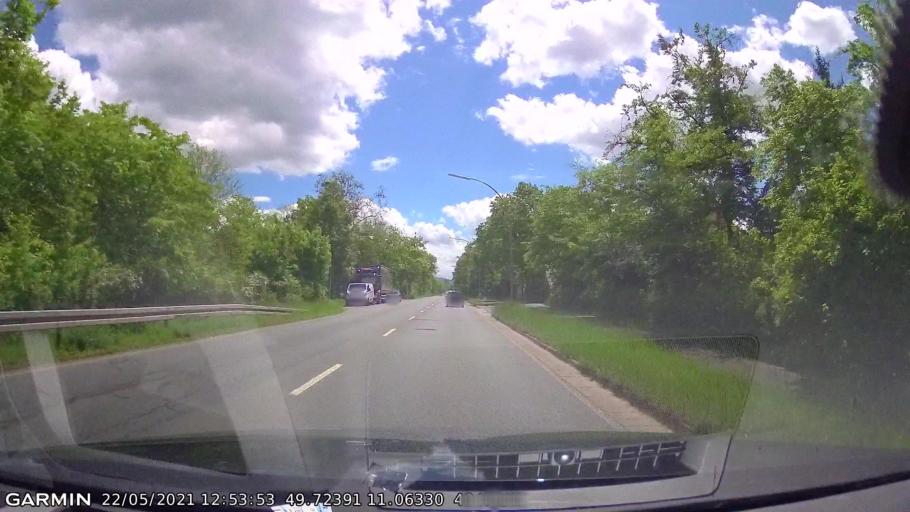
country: DE
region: Bavaria
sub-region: Upper Franconia
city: Forchheim
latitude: 49.7237
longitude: 11.0635
